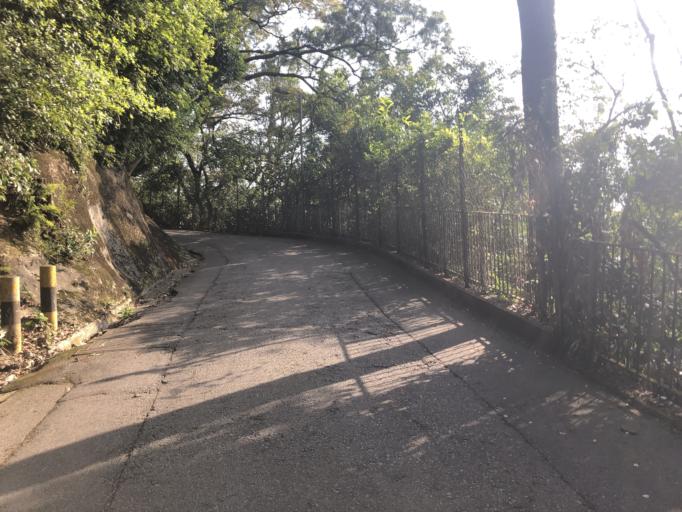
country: HK
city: Hong Kong
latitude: 22.2765
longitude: 114.1204
